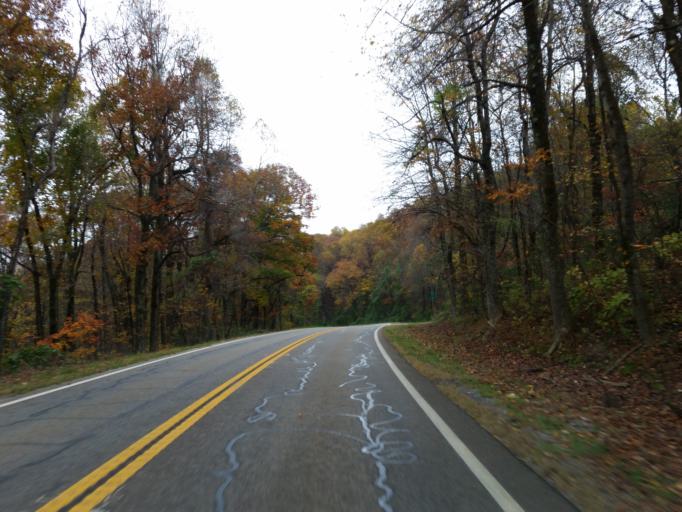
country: US
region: Georgia
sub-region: Pickens County
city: Jasper
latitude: 34.5429
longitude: -84.3564
